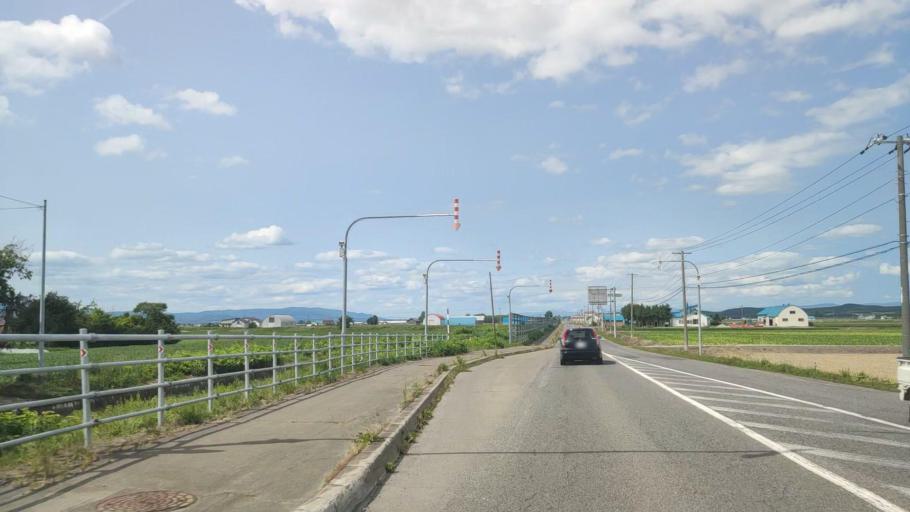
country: JP
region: Hokkaido
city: Nayoro
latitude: 44.1914
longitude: 142.4158
